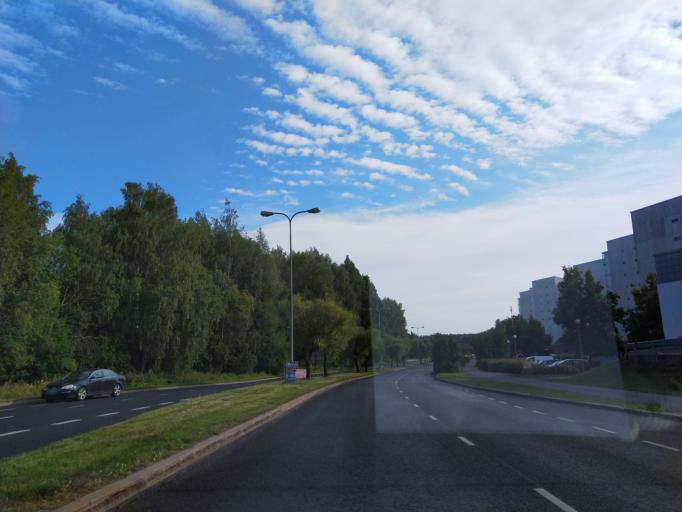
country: FI
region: Varsinais-Suomi
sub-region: Turku
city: Turku
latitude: 60.4299
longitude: 22.2403
